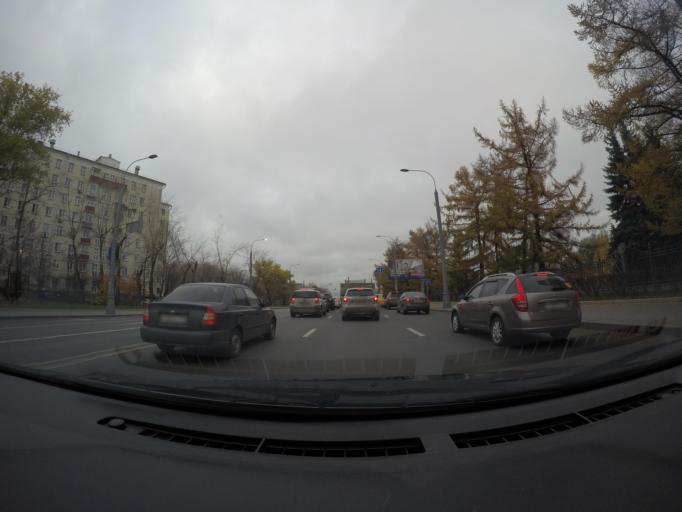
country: RU
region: Moscow
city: Ostankinskiy
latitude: 55.8202
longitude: 37.6372
